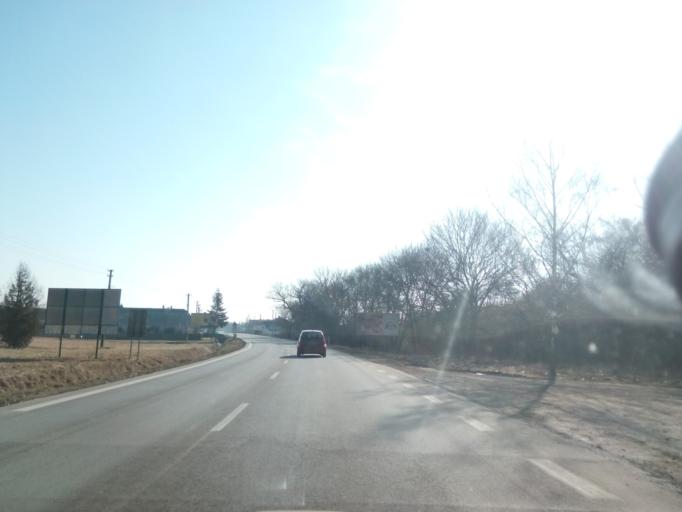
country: SK
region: Kosicky
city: Secovce
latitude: 48.7345
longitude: 21.5733
